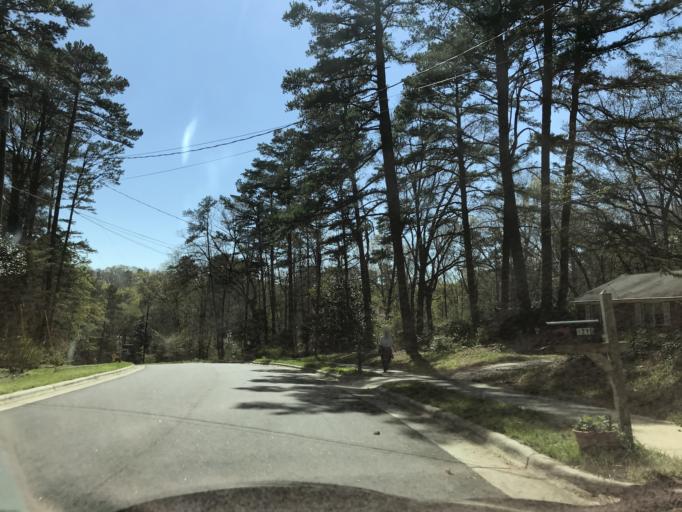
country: US
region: North Carolina
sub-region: Wake County
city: West Raleigh
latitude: 35.7816
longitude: -78.6976
